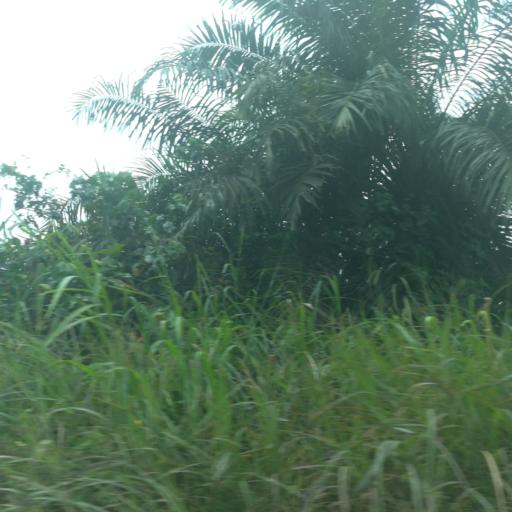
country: NG
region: Lagos
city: Ejirin
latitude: 6.6685
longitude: 3.7945
